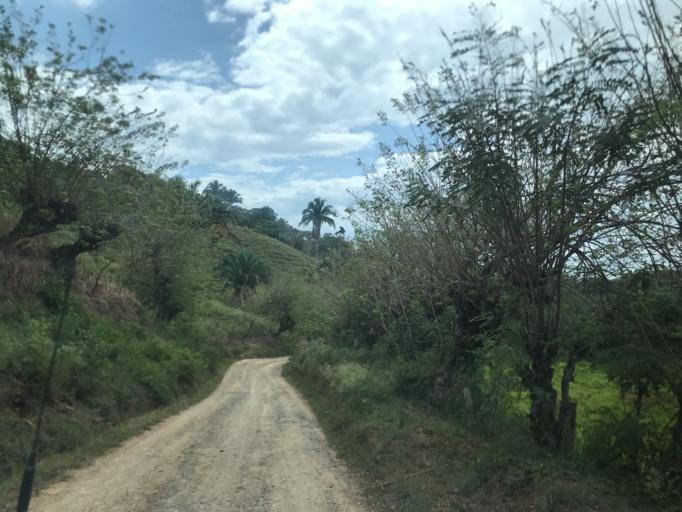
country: CO
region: Valle del Cauca
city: Obando
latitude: 4.5580
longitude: -75.9488
